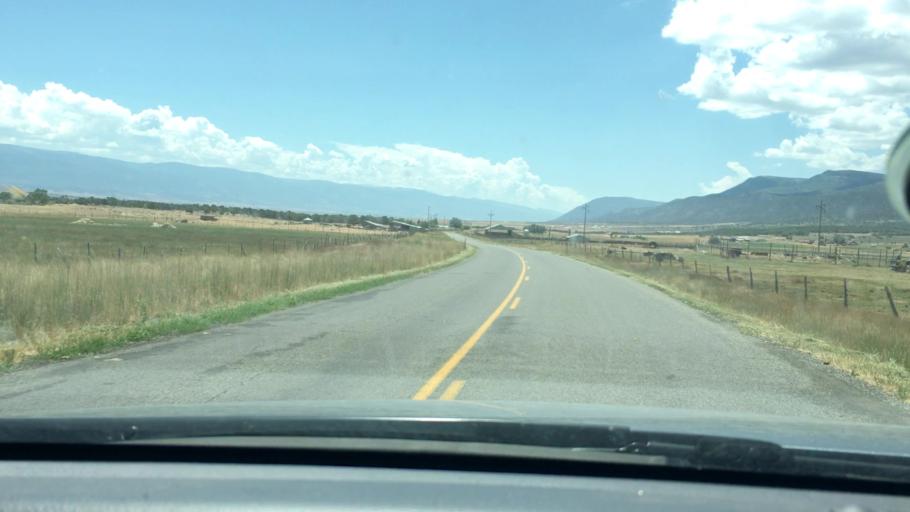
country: US
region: Utah
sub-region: Sanpete County
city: Fountain Green
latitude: 39.6136
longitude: -111.6448
